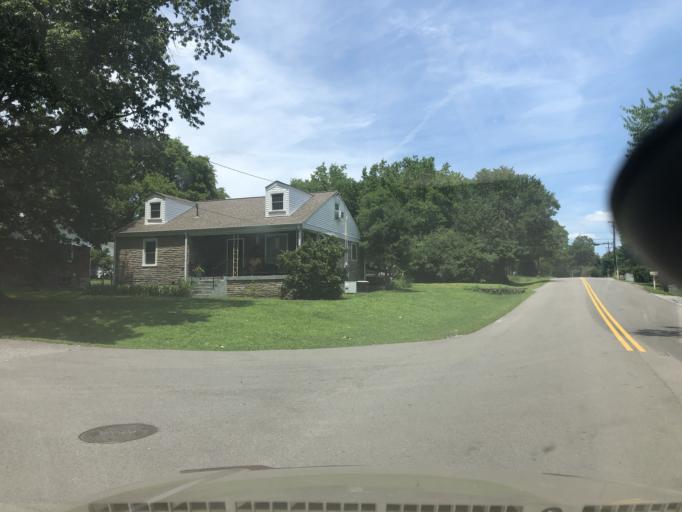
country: US
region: Tennessee
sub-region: Davidson County
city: Lakewood
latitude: 36.2568
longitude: -86.6952
